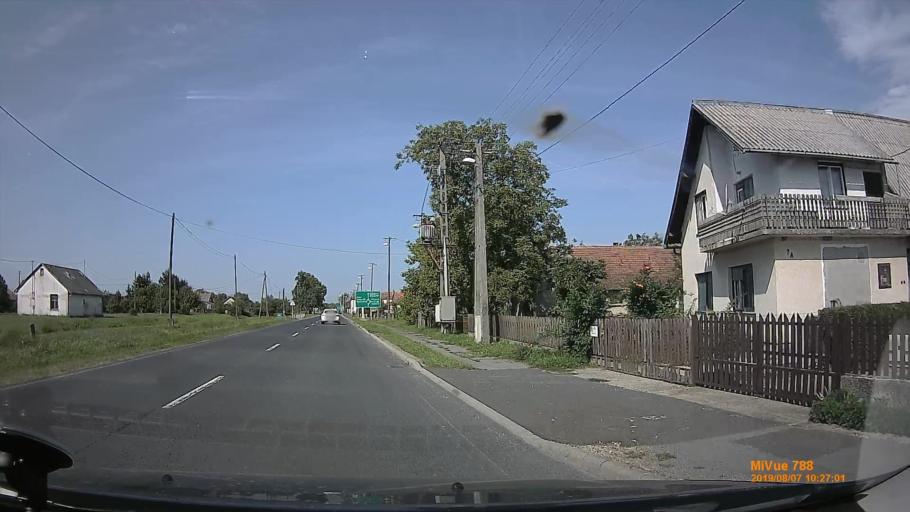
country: SI
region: Lendava-Lendva
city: Lendava
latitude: 46.6184
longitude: 16.4704
